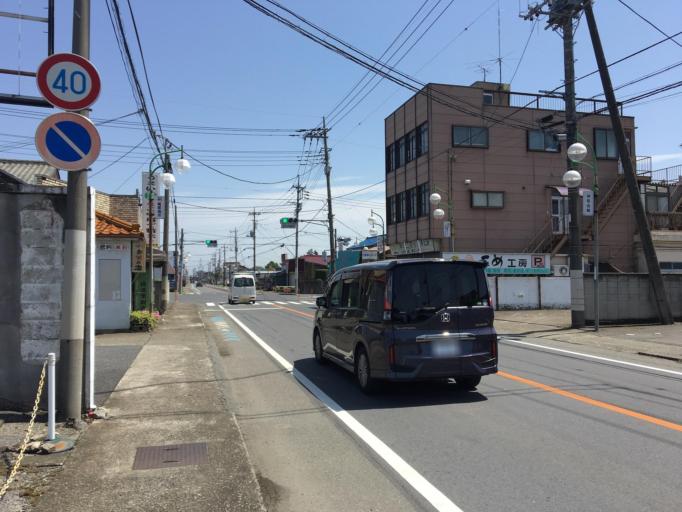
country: JP
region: Gunma
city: Sakai-nakajima
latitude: 36.2796
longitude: 139.3050
